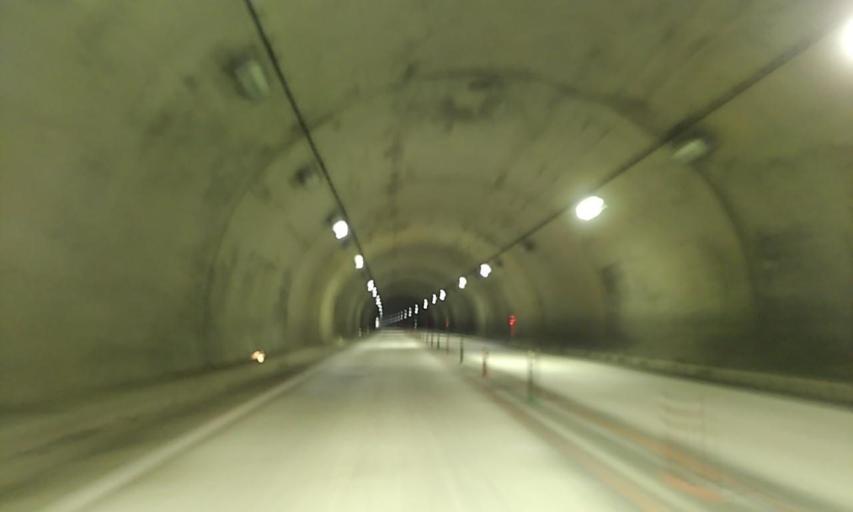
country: JP
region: Wakayama
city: Shingu
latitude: 33.6011
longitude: 135.9161
